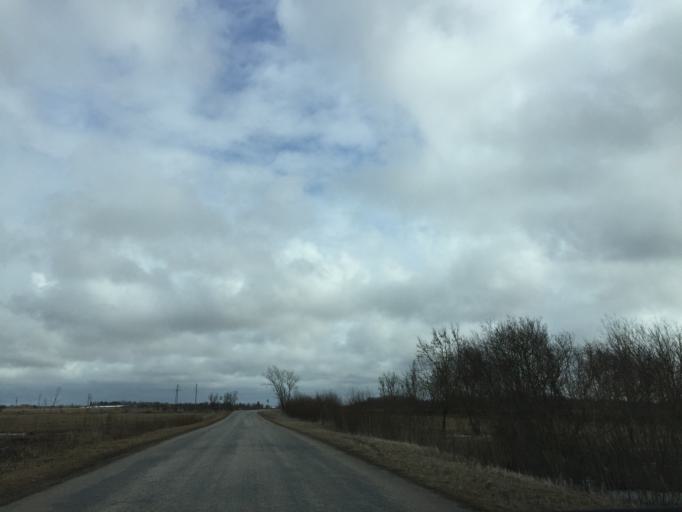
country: EE
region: Laeaene
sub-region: Lihula vald
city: Lihula
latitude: 58.7273
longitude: 23.9059
